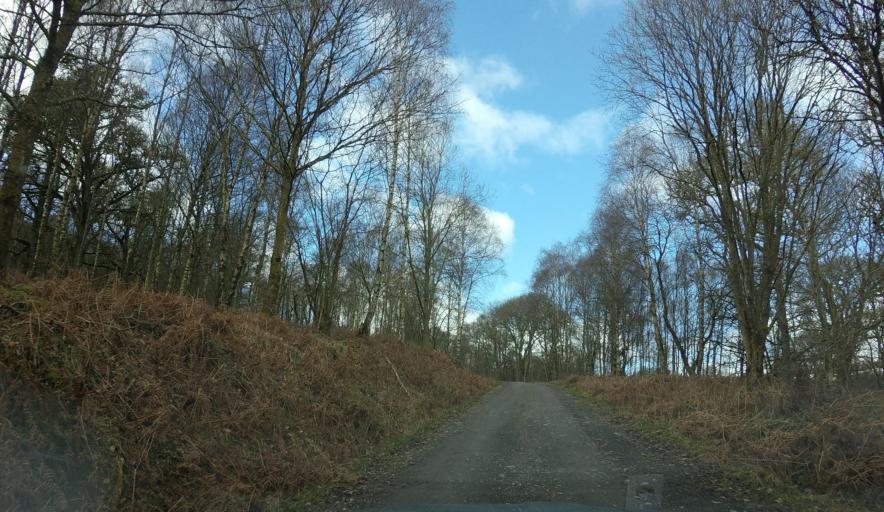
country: GB
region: Scotland
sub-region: Perth and Kinross
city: Pitlochry
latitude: 56.6506
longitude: -3.7402
